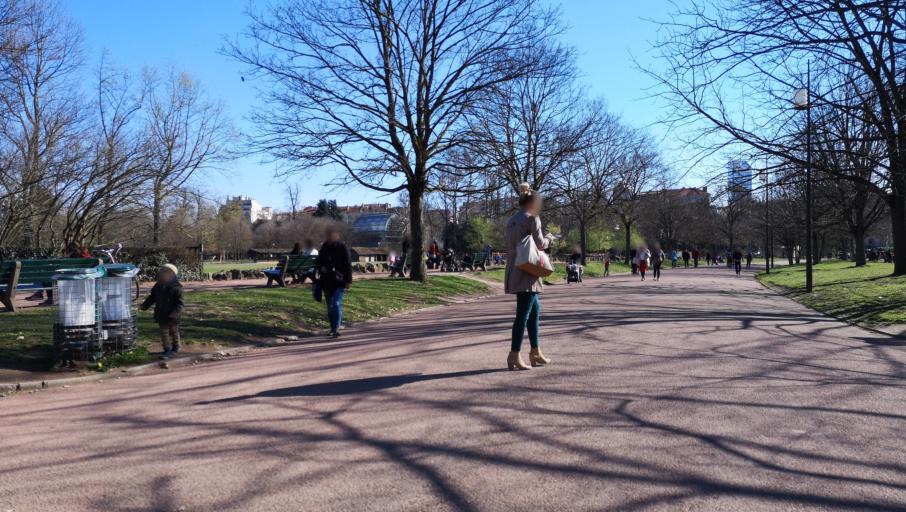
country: FR
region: Rhone-Alpes
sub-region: Departement du Rhone
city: Caluire-et-Cuire
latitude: 45.7760
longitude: 4.8532
